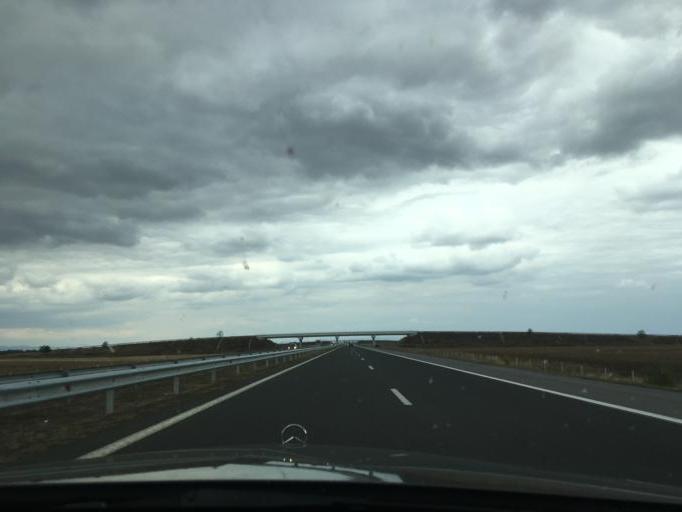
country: BG
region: Stara Zagora
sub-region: Obshtina Stara Zagora
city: Stara Zagora
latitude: 42.3640
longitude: 25.7721
